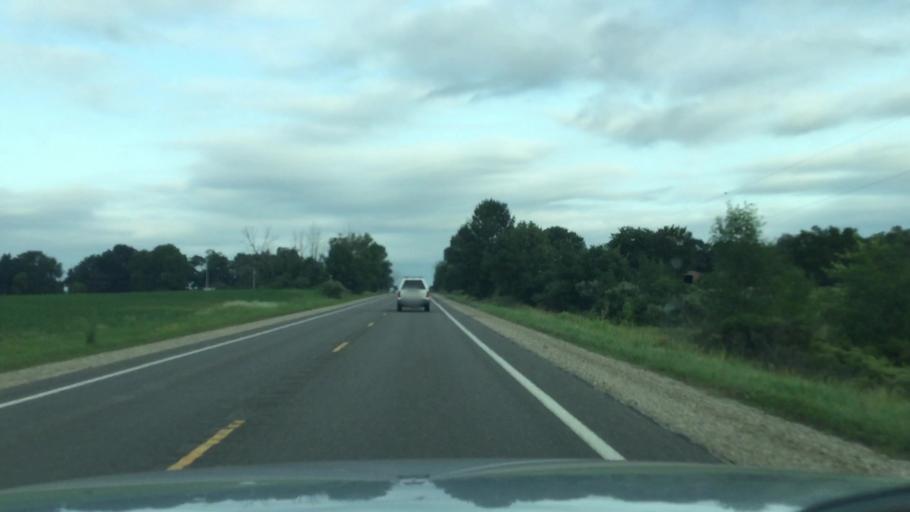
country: US
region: Michigan
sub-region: Montcalm County
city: Stanton
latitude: 43.1775
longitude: -85.0247
